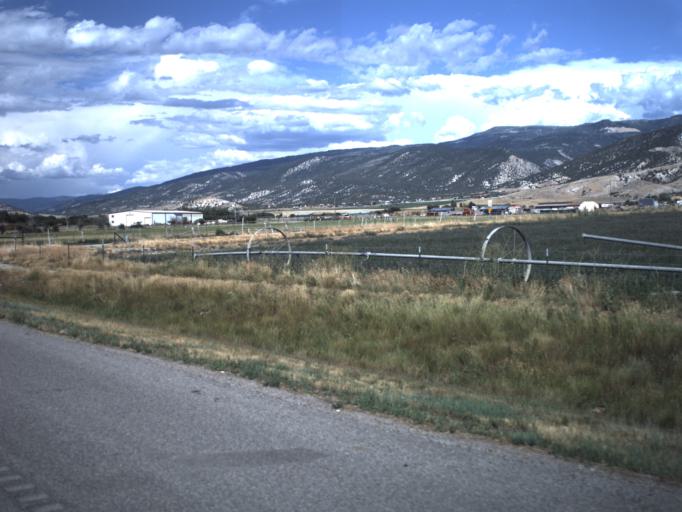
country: US
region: Utah
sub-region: Sanpete County
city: Ephraim
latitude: 39.3281
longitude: -111.6015
